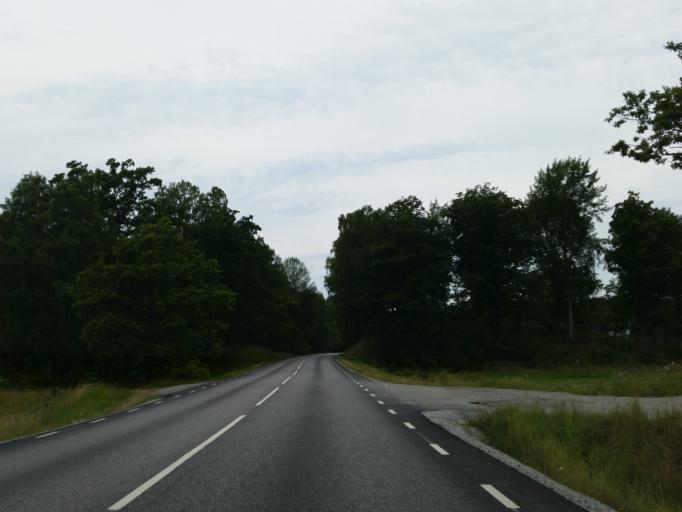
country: SE
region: Stockholm
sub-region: Salems Kommun
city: Ronninge
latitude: 59.2301
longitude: 17.7173
